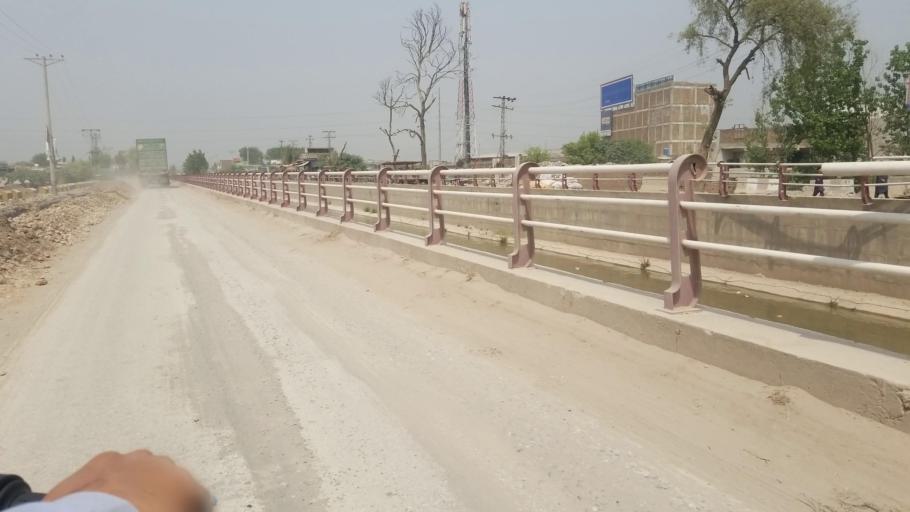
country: PK
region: Khyber Pakhtunkhwa
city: Peshawar
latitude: 33.9677
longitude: 71.5398
